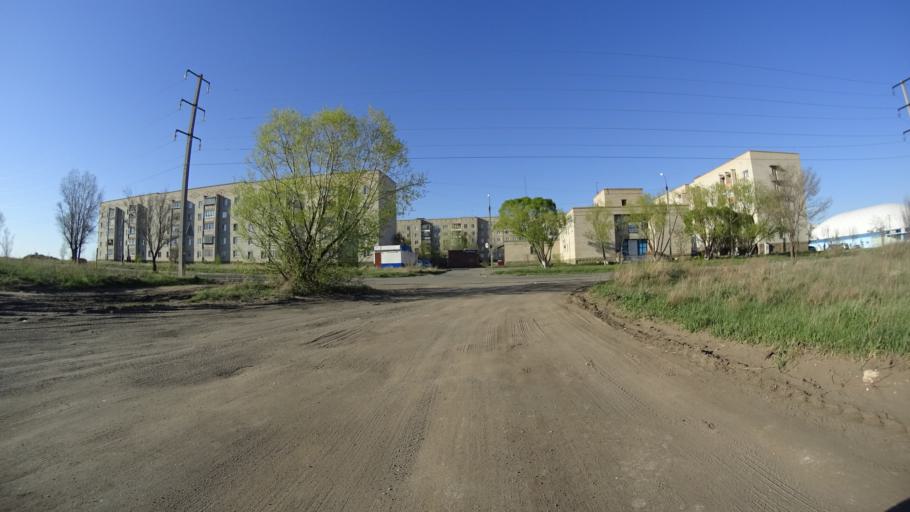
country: RU
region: Chelyabinsk
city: Troitsk
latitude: 54.0774
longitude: 61.5227
